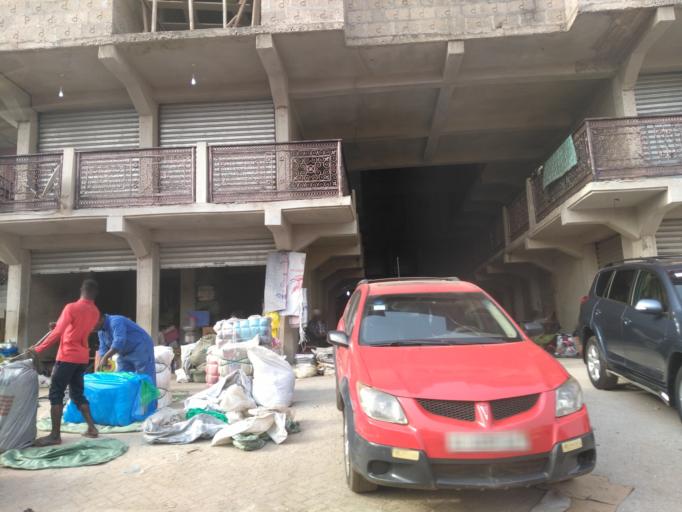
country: GH
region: Ashanti
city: Kumasi
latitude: 6.7011
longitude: -1.6196
